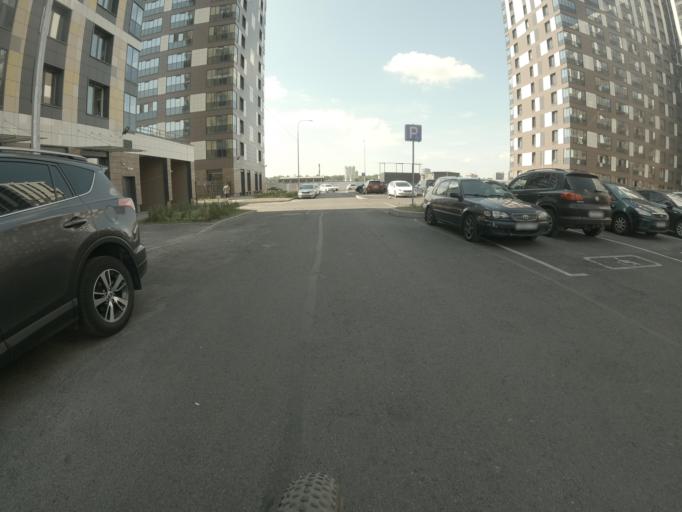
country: RU
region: St.-Petersburg
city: Obukhovo
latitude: 59.9067
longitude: 30.4420
